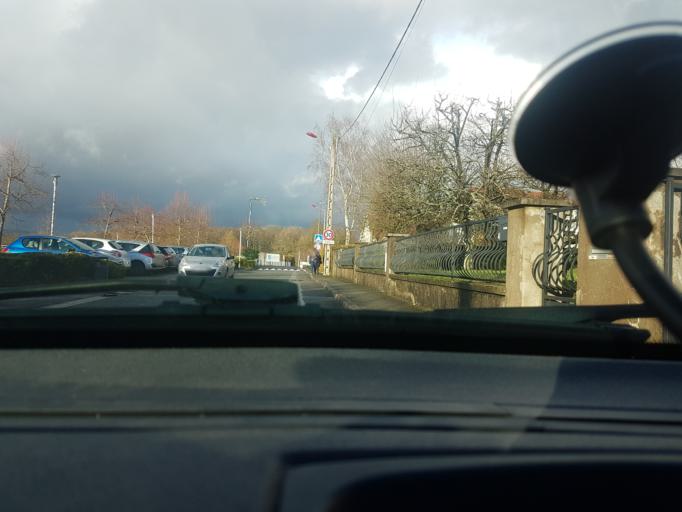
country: FR
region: Franche-Comte
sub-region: Territoire de Belfort
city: Andelnans
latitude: 47.5873
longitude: 6.8671
